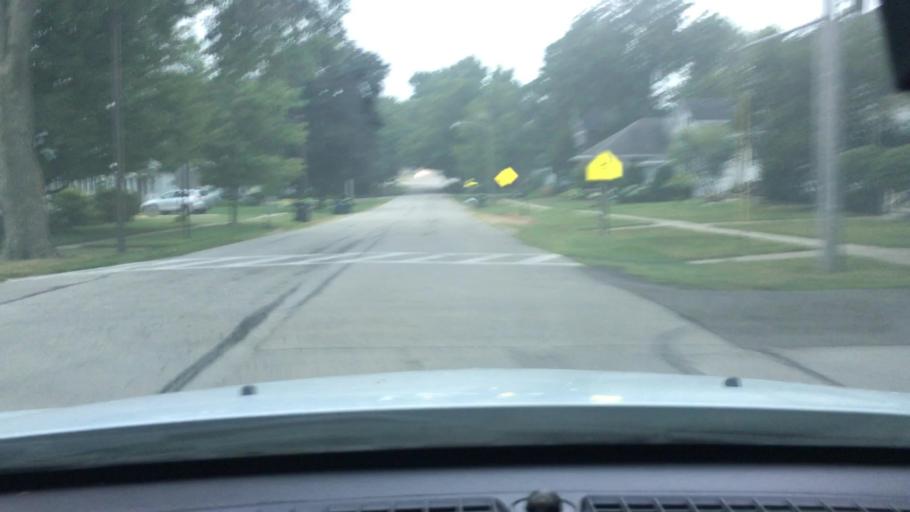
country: US
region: Illinois
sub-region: DeKalb County
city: Waterman
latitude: 41.7716
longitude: -88.7739
